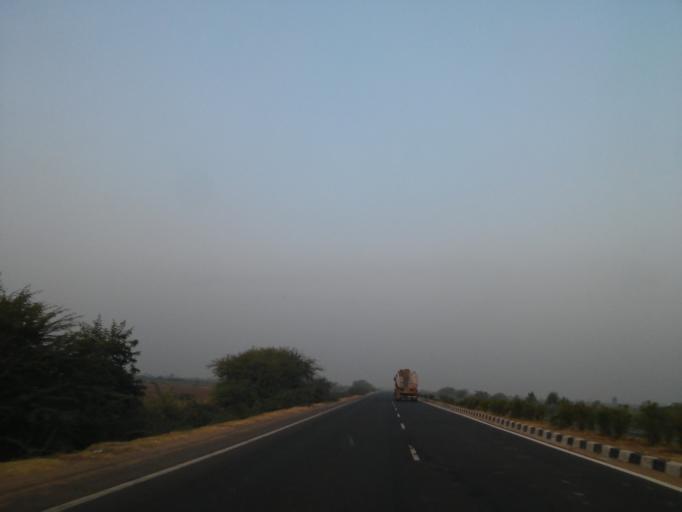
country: IN
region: Gujarat
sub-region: Surendranagar
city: Halvad
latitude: 23.0244
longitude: 70.9779
